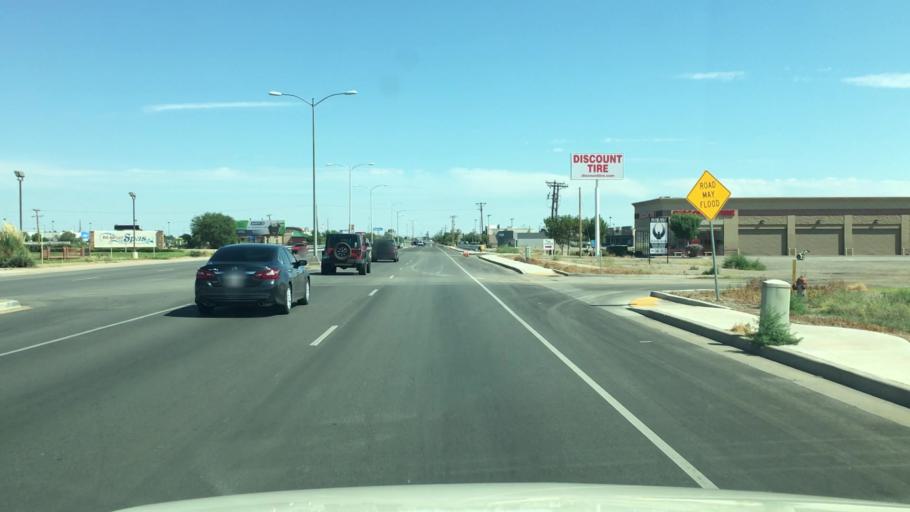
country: US
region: New Mexico
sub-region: Chaves County
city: Roswell
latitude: 33.4434
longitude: -104.5232
